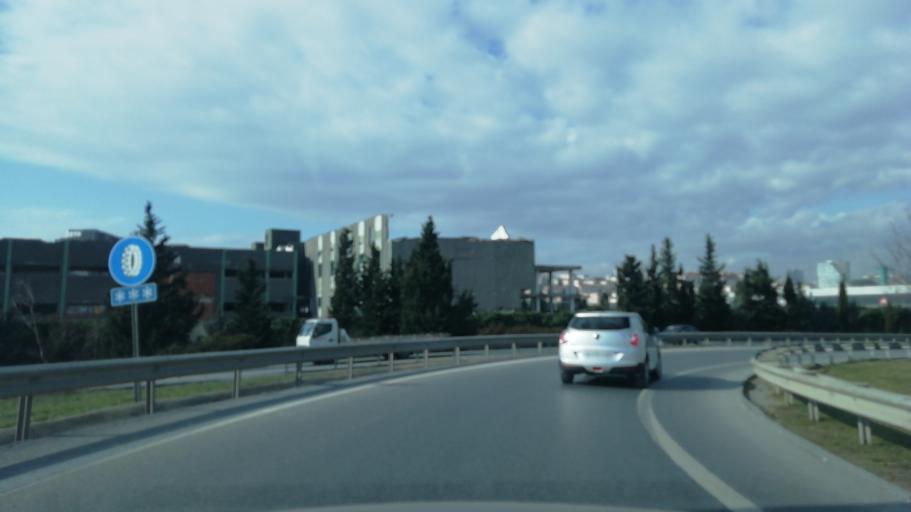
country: TR
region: Istanbul
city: Mahmutbey
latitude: 41.0094
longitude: 28.8123
